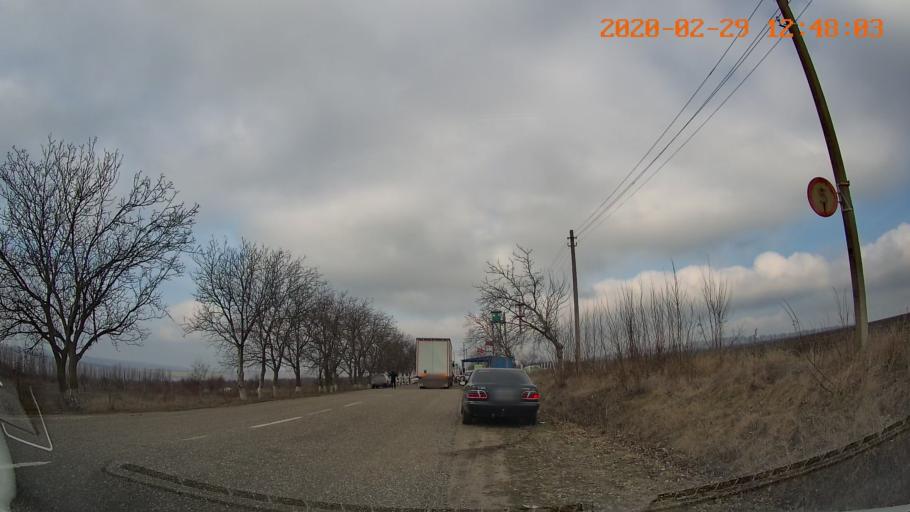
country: MD
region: Telenesti
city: Camenca
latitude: 48.1280
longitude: 28.7412
